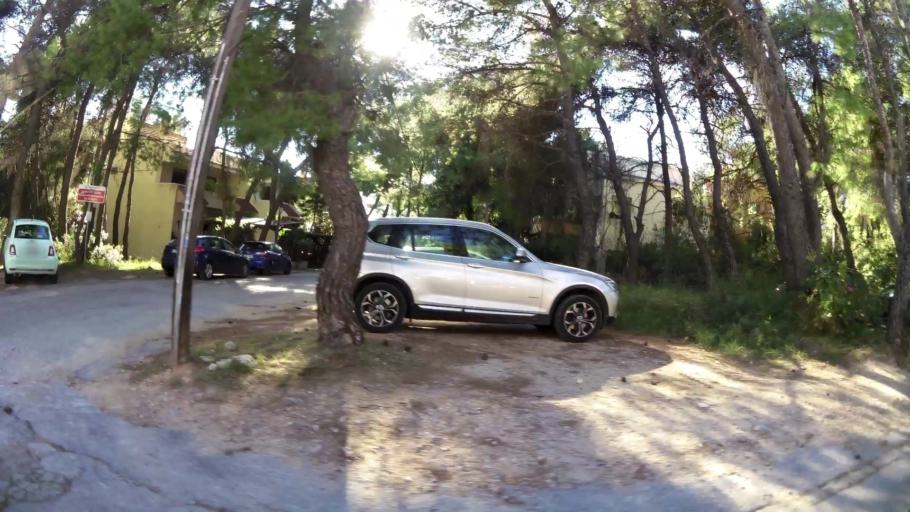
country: GR
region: Attica
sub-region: Nomarchia Athinas
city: Ekali
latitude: 38.1214
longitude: 23.8444
